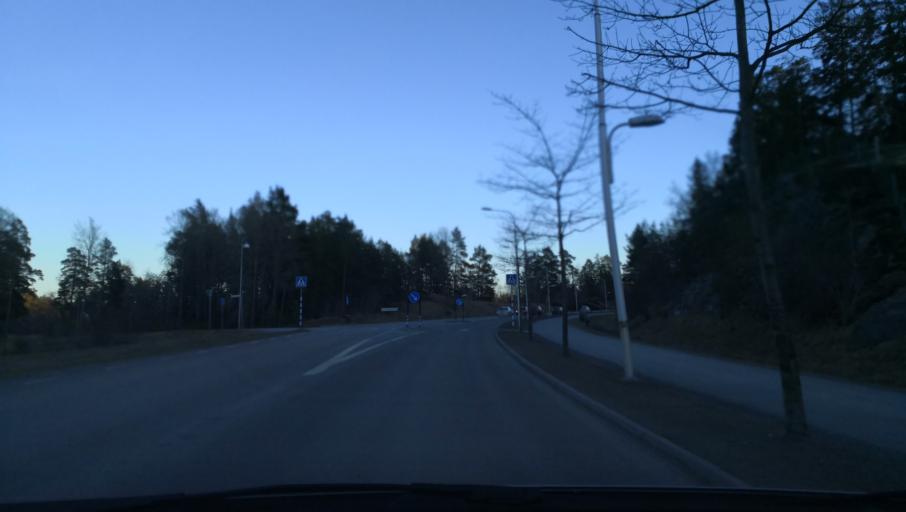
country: SE
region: Stockholm
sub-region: Varmdo Kommun
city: Gustavsberg
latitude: 59.3168
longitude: 18.3908
